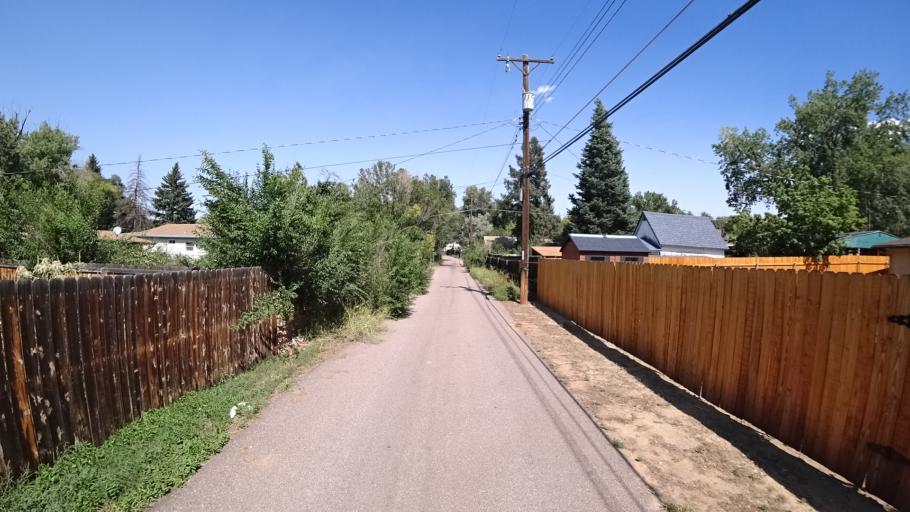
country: US
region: Colorado
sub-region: El Paso County
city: Colorado Springs
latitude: 38.8805
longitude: -104.8057
